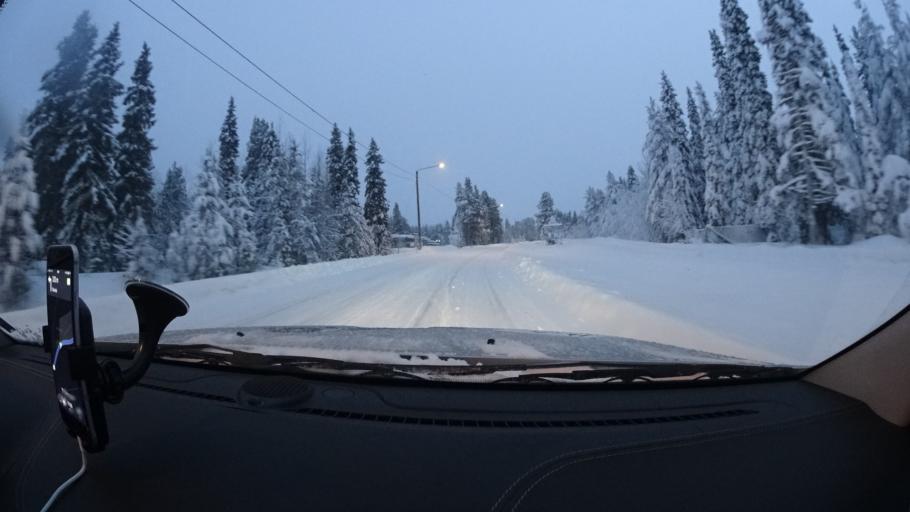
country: FI
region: Lapland
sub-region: Tunturi-Lappi
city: Kittilae
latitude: 67.6713
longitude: 24.8742
